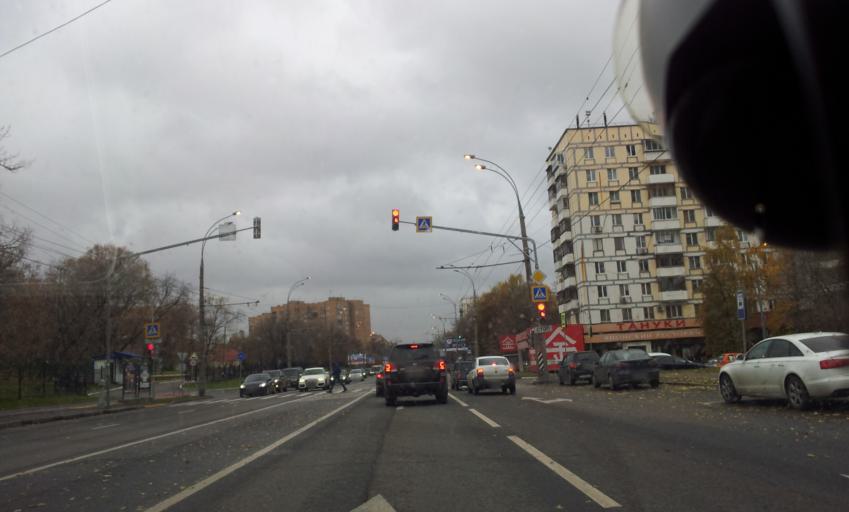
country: RU
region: Moscow
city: Vorob'yovo
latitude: 55.7216
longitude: 37.5264
